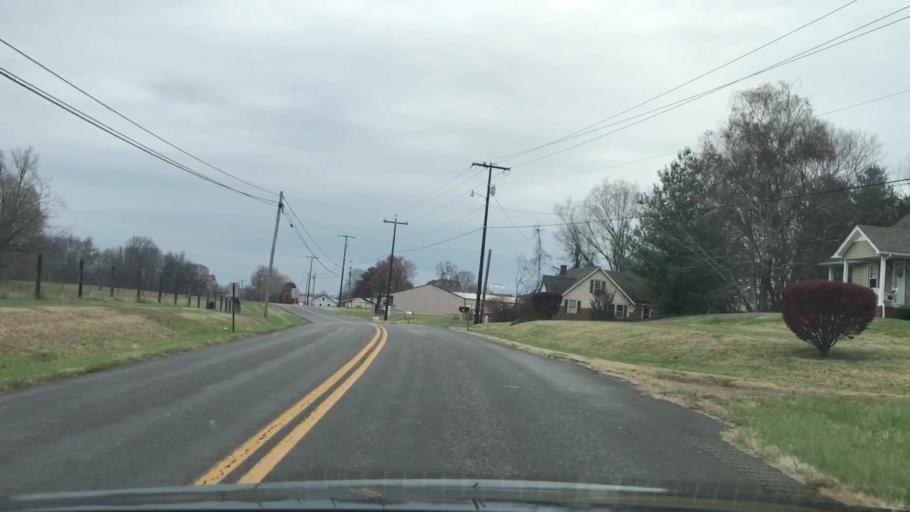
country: US
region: Kentucky
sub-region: Metcalfe County
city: Edmonton
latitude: 36.9715
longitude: -85.6090
